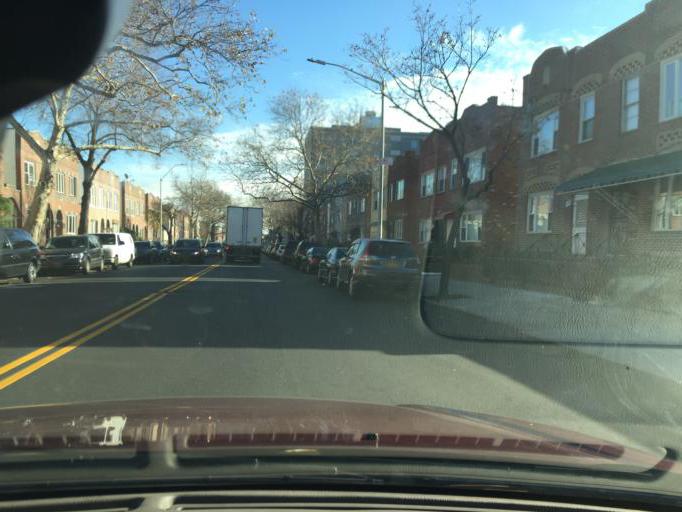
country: US
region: New York
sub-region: Kings County
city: Bensonhurst
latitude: 40.6179
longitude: -73.9805
